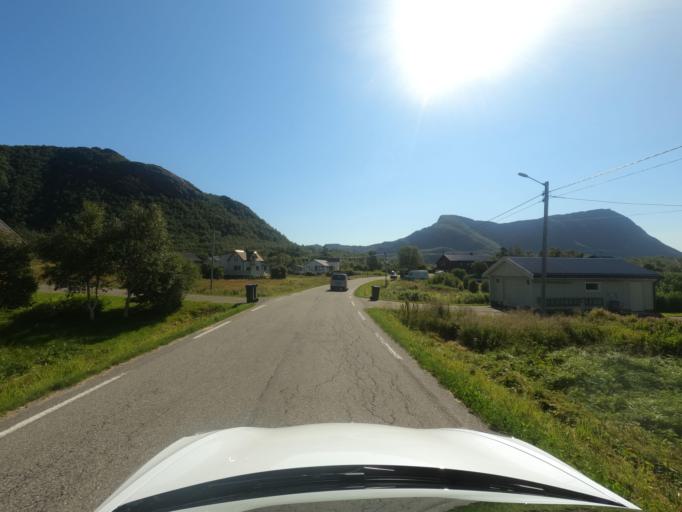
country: NO
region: Nordland
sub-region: Hadsel
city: Stokmarknes
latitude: 68.3097
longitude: 14.9918
